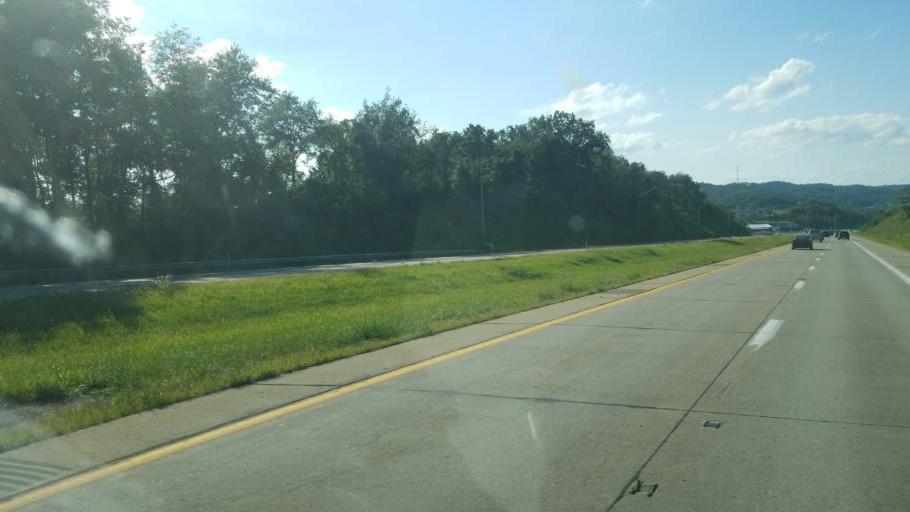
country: US
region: Pennsylvania
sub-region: Greene County
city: Morrisville
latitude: 39.8940
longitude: -80.1387
